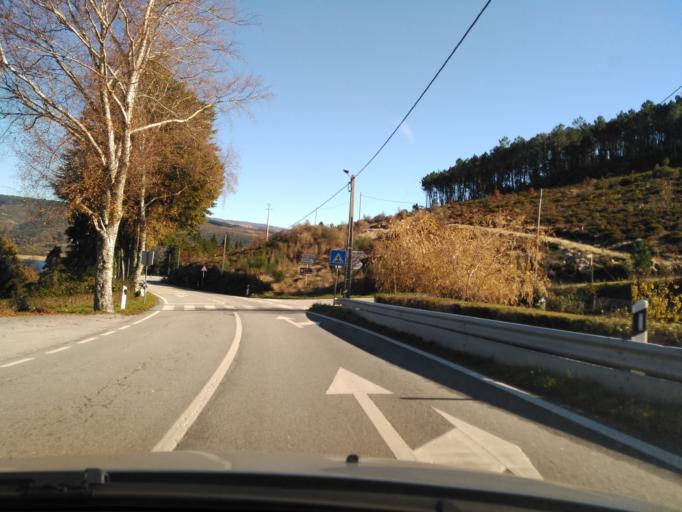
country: PT
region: Braga
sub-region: Cabeceiras de Basto
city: Cabeceiras de Basto
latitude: 41.6723
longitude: -7.9742
